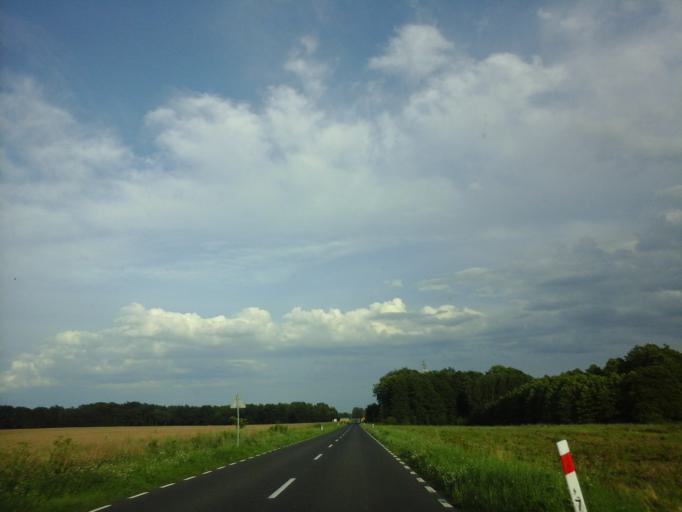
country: PL
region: West Pomeranian Voivodeship
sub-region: Powiat kamienski
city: Swierzno
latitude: 53.8908
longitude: 14.8741
